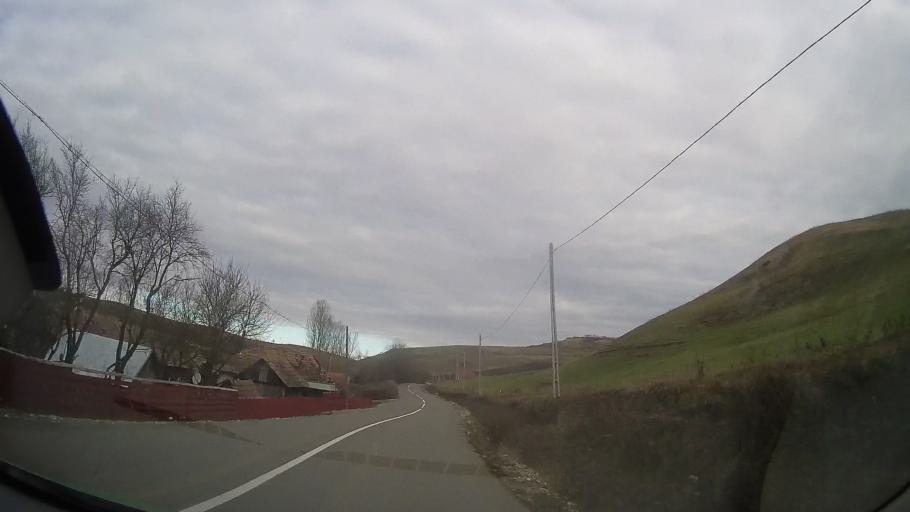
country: RO
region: Bistrita-Nasaud
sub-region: Comuna Silvasu de Campie
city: Silvasu de Campie
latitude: 46.8113
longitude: 24.2954
